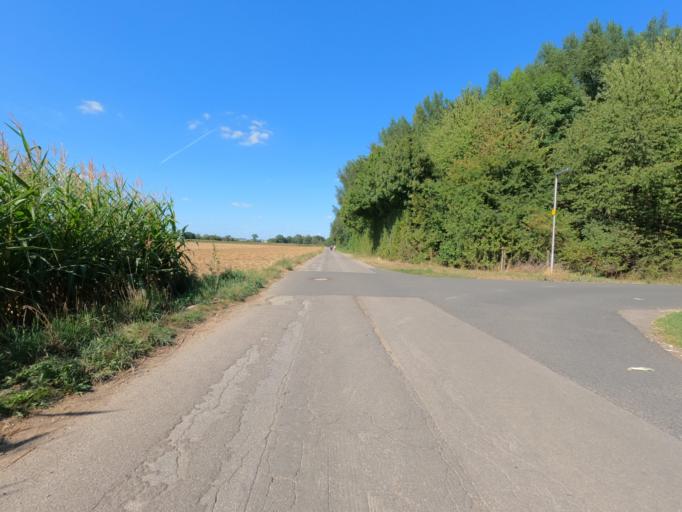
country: DE
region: North Rhine-Westphalia
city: Julich
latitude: 50.9253
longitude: 6.3425
